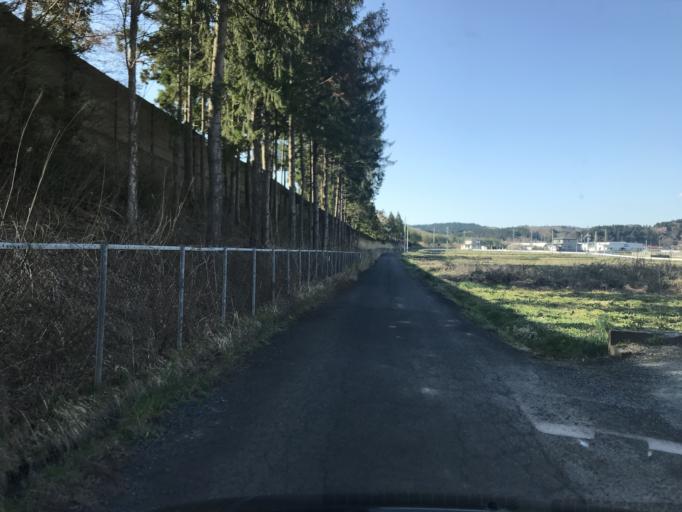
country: JP
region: Iwate
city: Ichinoseki
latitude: 38.9232
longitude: 141.1028
